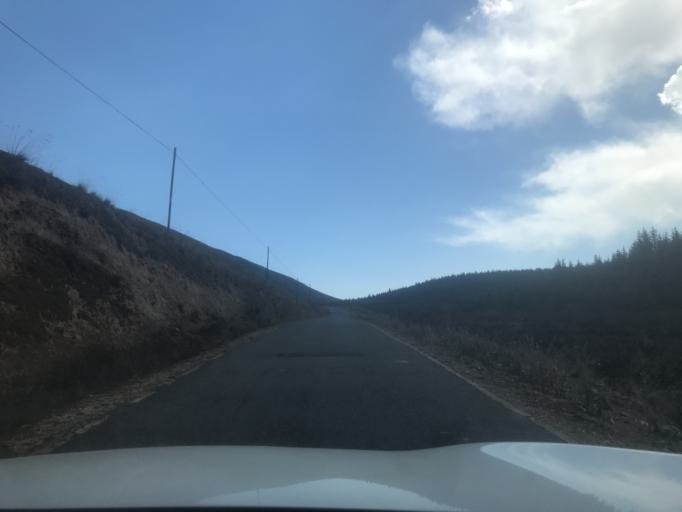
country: CN
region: Gansu Sheng
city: Gulang
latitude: 37.3692
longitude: 102.7545
